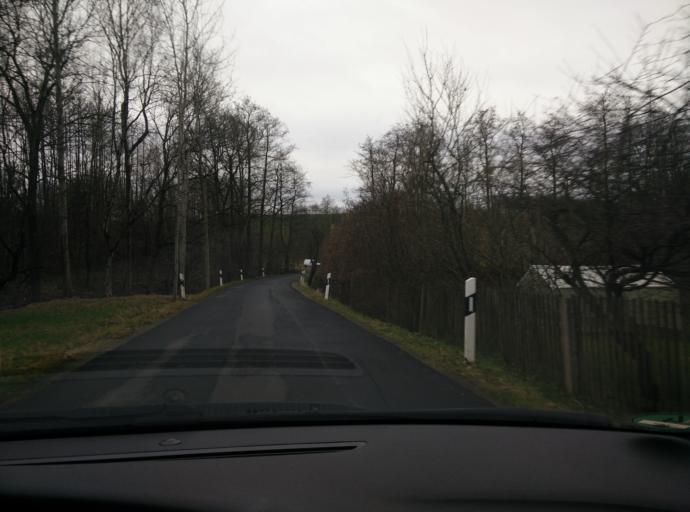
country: DE
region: Saxony
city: Frohburg
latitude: 51.0299
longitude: 12.6132
